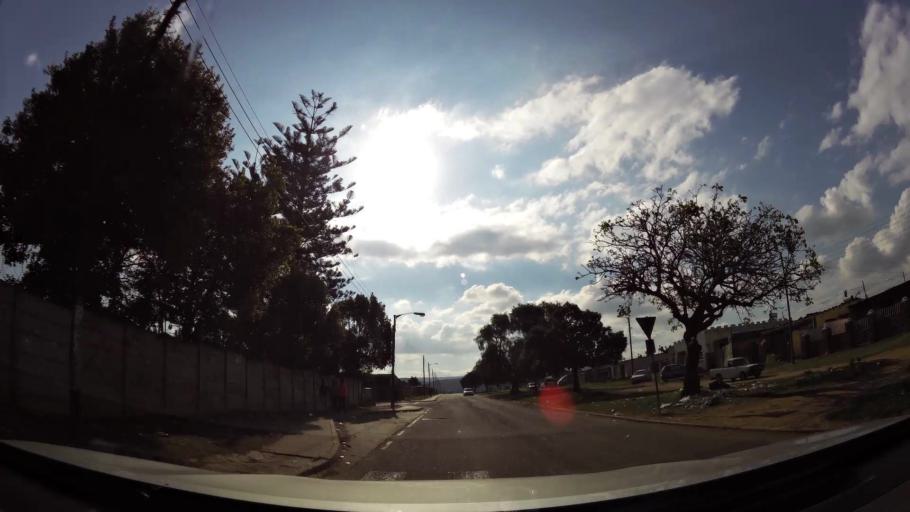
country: ZA
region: Eastern Cape
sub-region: Nelson Mandela Bay Metropolitan Municipality
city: Uitenhage
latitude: -33.7384
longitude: 25.3714
